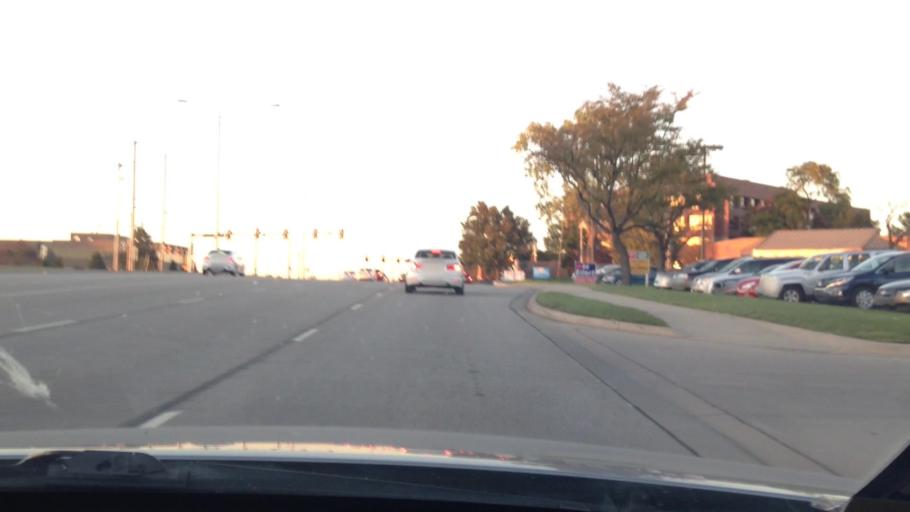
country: US
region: Kansas
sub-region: Johnson County
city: Lenexa
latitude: 38.9261
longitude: -94.7234
